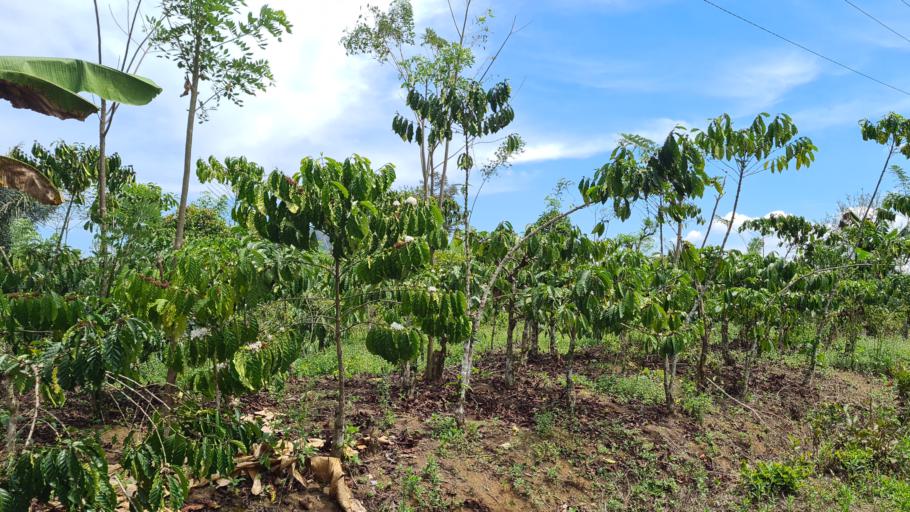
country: ID
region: Lampung
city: Kenali
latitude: -5.0968
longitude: 104.4341
